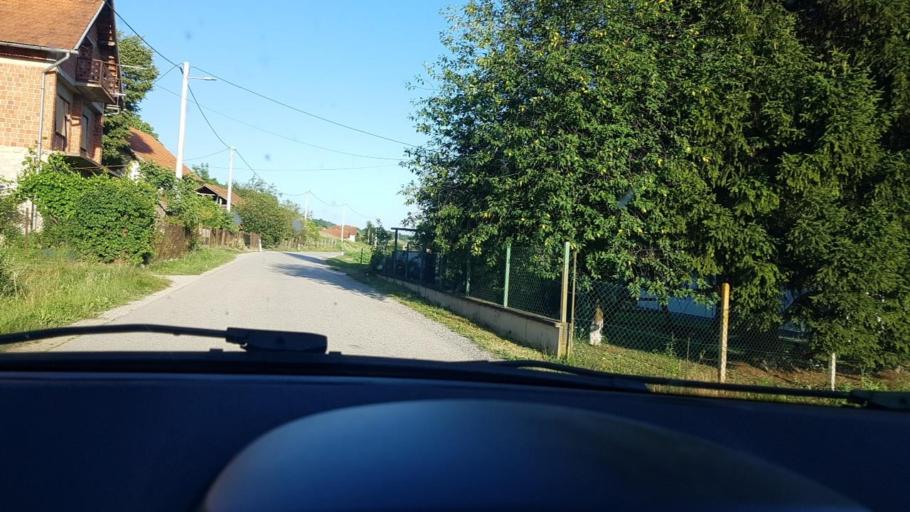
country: HR
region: Krapinsko-Zagorska
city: Mihovljan
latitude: 46.0843
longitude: 15.9710
